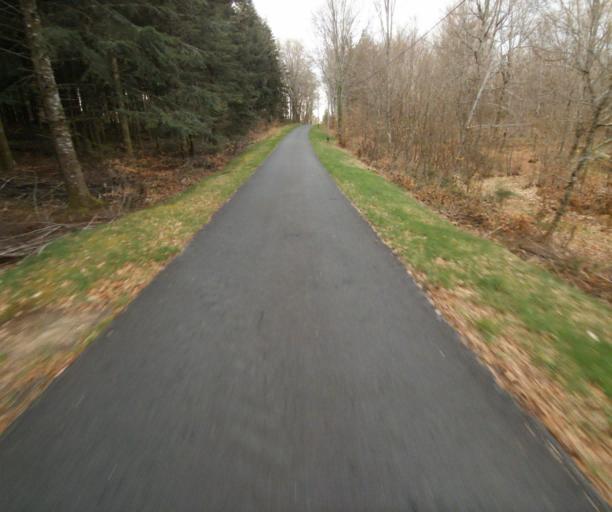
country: FR
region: Limousin
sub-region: Departement de la Correze
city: Argentat
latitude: 45.2191
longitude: 1.9561
